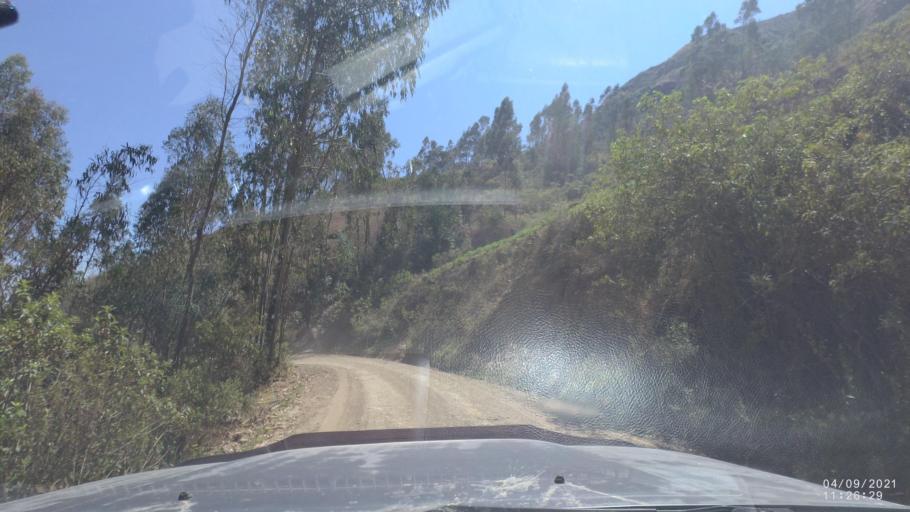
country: BO
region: Cochabamba
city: Colchani
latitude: -17.2530
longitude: -66.5139
